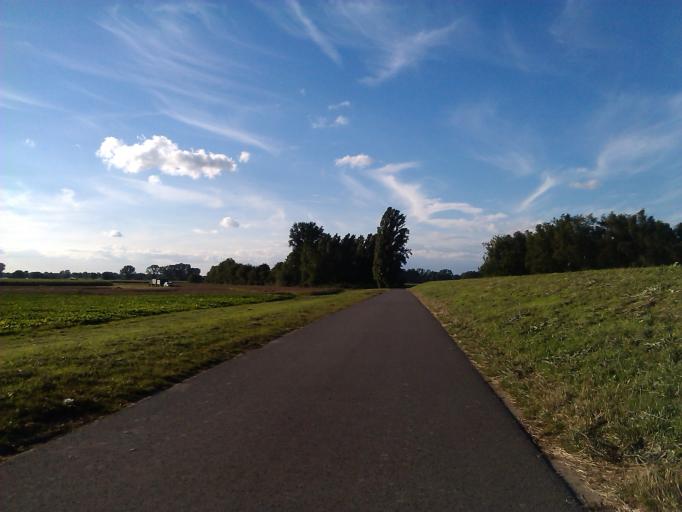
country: DE
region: Rheinland-Pfalz
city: Otterstadt
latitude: 49.3785
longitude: 8.4573
